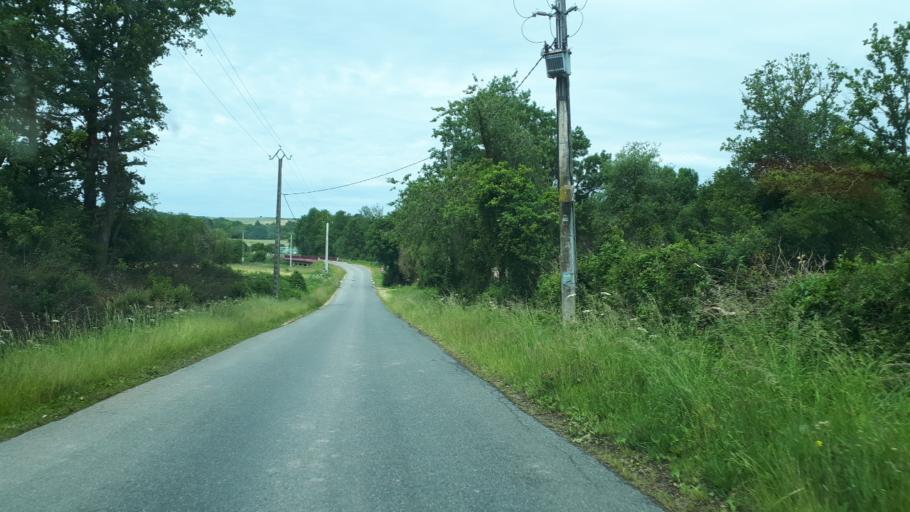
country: FR
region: Centre
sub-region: Departement du Cher
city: Savigny-en-Sancerre
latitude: 47.3955
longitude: 2.6617
